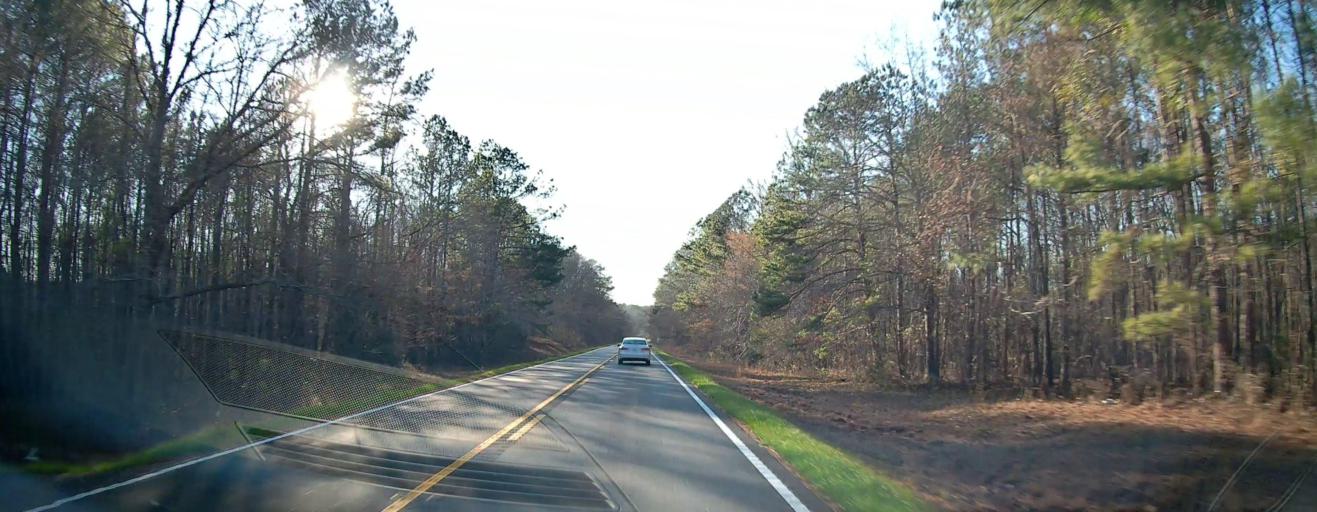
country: US
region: Georgia
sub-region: Harris County
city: Pine Mountain
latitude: 32.9151
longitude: -84.7553
